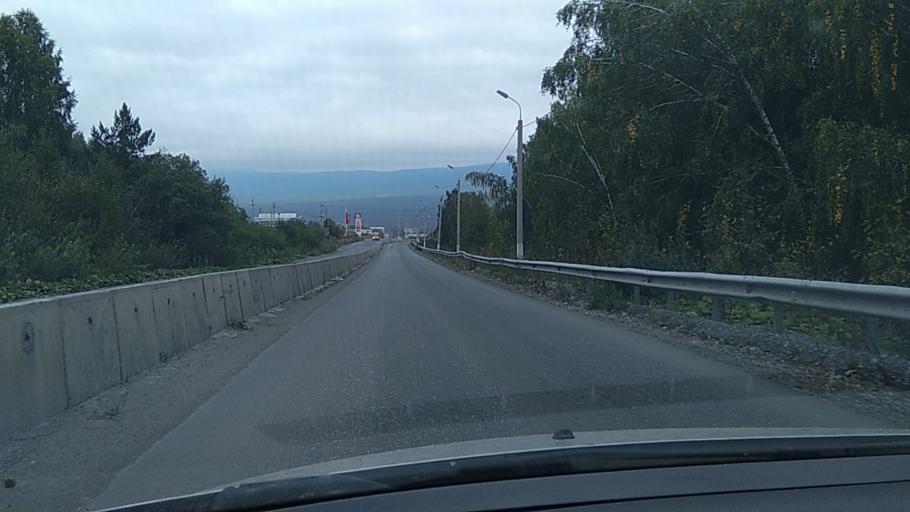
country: RU
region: Chelyabinsk
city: Zlatoust
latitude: 55.1170
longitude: 59.7396
